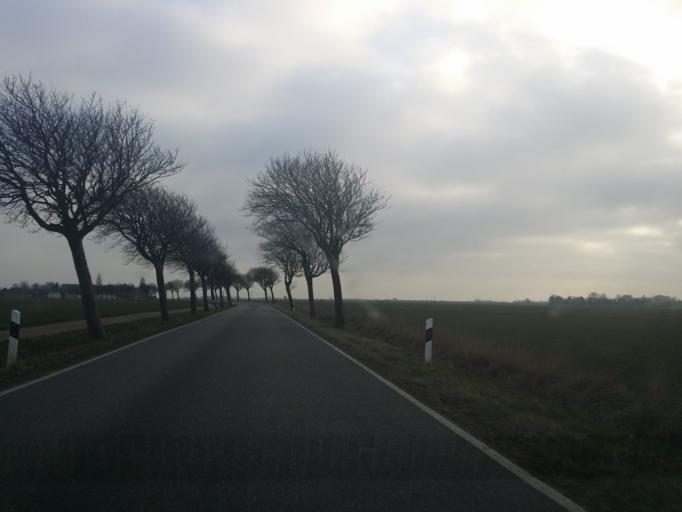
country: DE
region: Schleswig-Holstein
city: Grossenbrode
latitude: 54.4651
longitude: 11.0453
